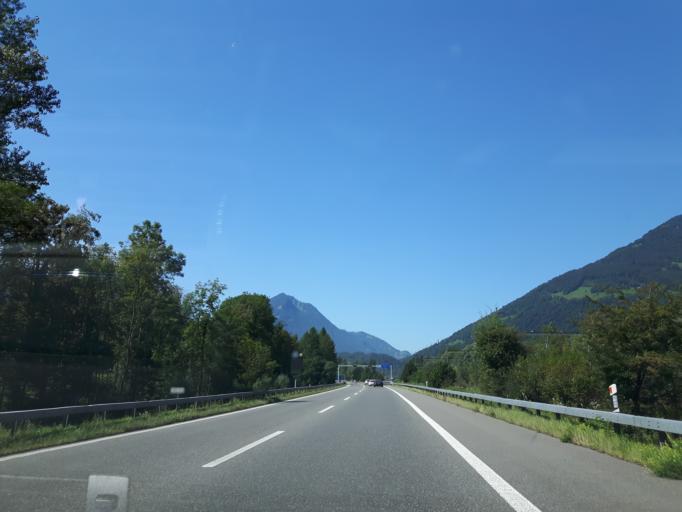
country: CH
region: Saint Gallen
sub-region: Wahlkreis See-Gaster
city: Weesen
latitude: 47.1259
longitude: 9.1138
